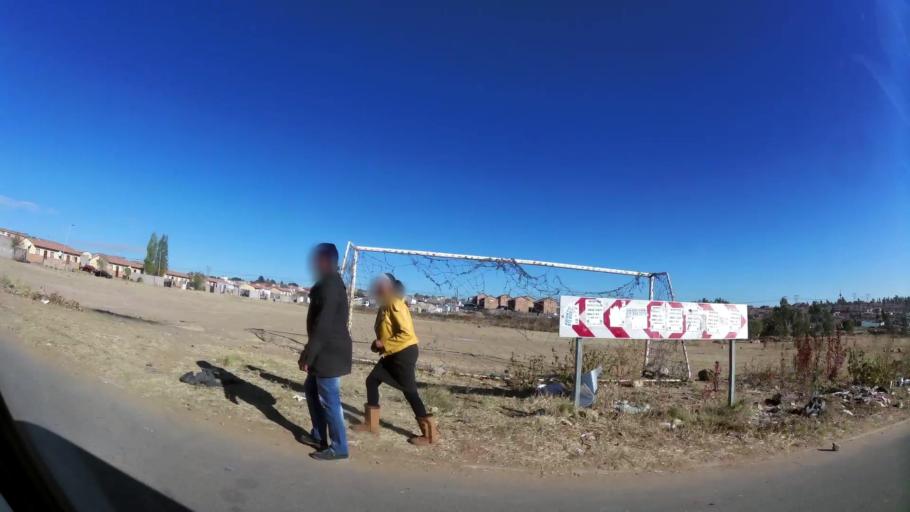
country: ZA
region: Gauteng
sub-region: City of Johannesburg Metropolitan Municipality
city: Diepsloot
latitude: -25.9007
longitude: 28.0916
